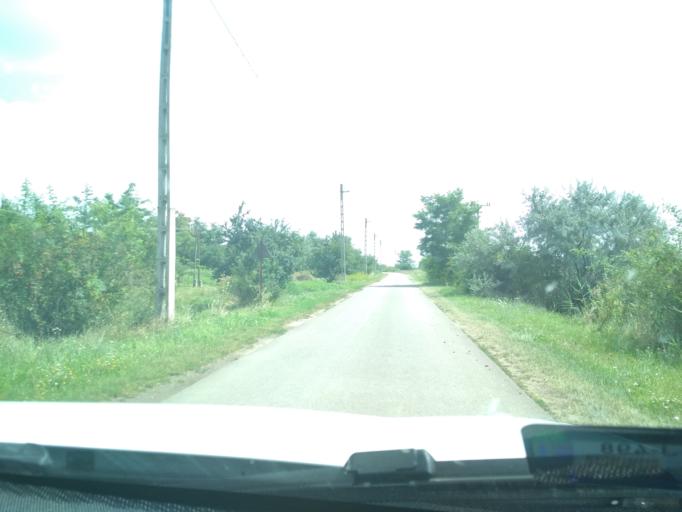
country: HU
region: Jasz-Nagykun-Szolnok
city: Abadszalok
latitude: 47.4673
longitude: 20.5860
